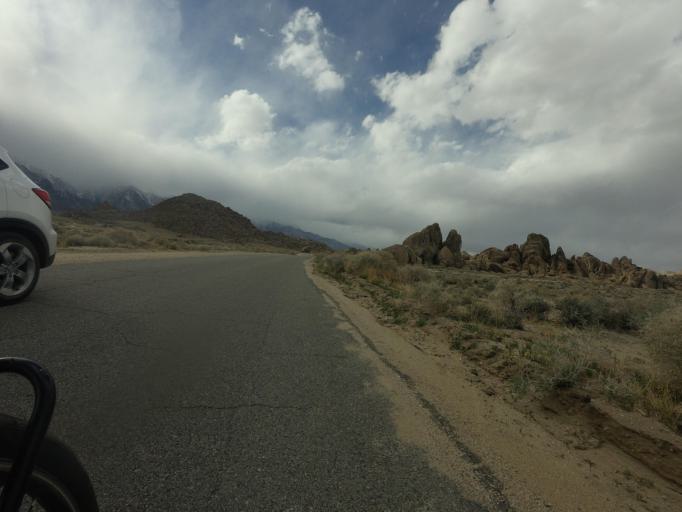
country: US
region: California
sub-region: Inyo County
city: Lone Pine
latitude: 36.5981
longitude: -118.1149
